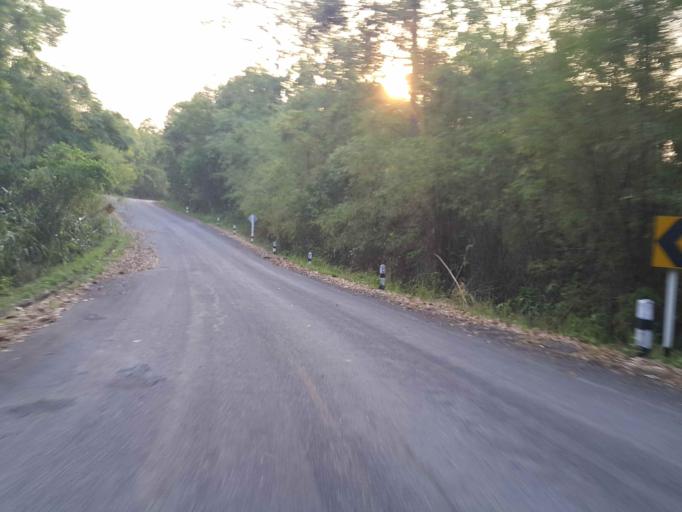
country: TH
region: Chiang Mai
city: Mae On
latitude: 19.0076
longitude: 99.3143
